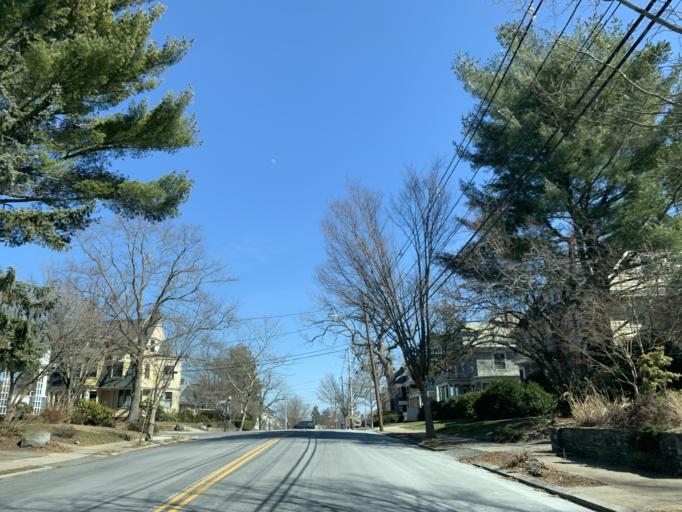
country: US
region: Rhode Island
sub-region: Providence County
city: Providence
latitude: 41.8358
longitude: -71.3995
